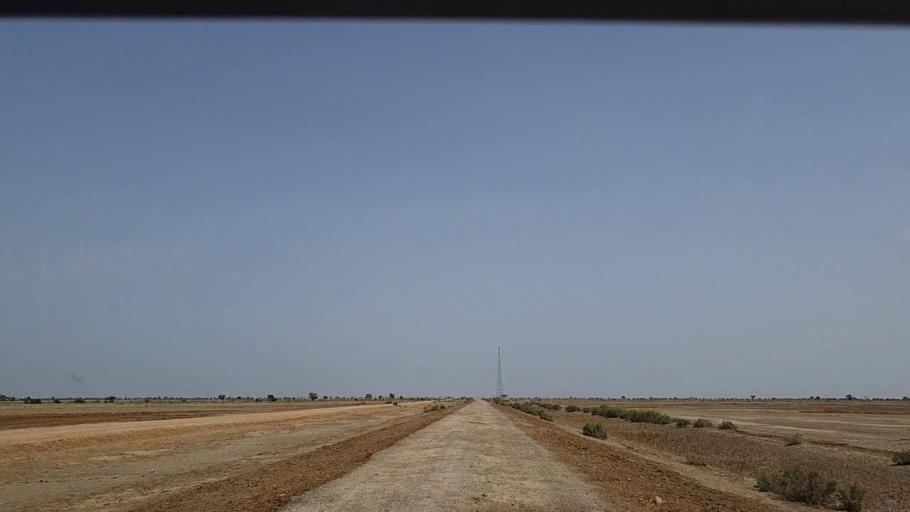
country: PK
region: Sindh
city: Phulji
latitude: 26.7965
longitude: 67.6384
